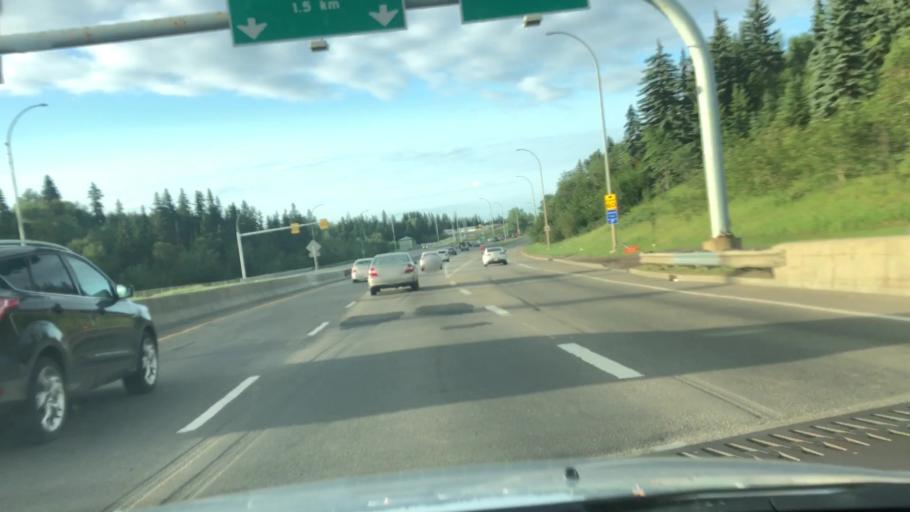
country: CA
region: Alberta
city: Edmonton
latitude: 53.5545
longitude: -113.4385
